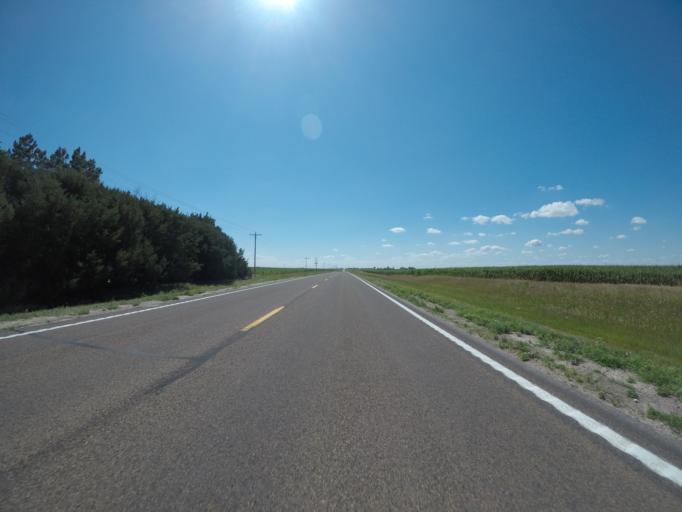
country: US
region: Nebraska
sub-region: Chase County
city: Imperial
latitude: 40.5376
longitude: -101.7345
